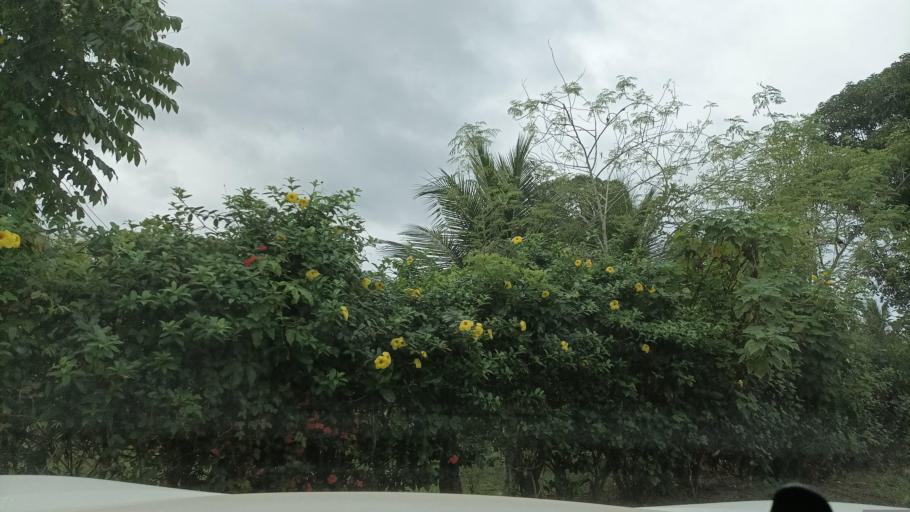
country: MX
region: Veracruz
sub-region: Cosoleacaque
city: Coacotla
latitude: 17.9431
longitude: -94.7057
